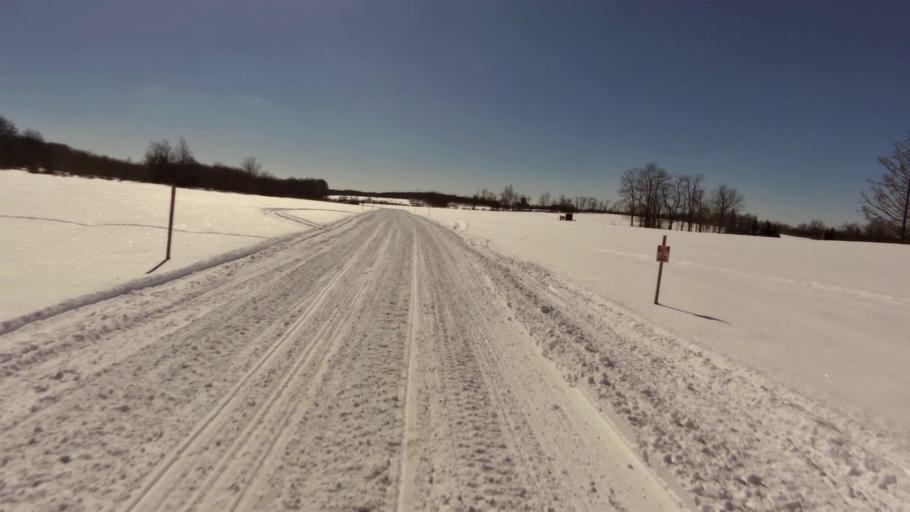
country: US
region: New York
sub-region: Chautauqua County
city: Mayville
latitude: 42.2274
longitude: -79.3942
